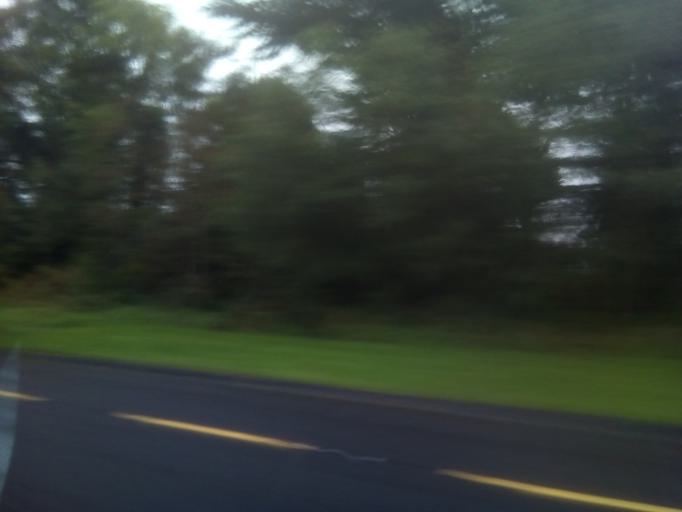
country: IE
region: Leinster
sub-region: An Longfort
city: Edgeworthstown
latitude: 53.6968
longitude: -7.6241
